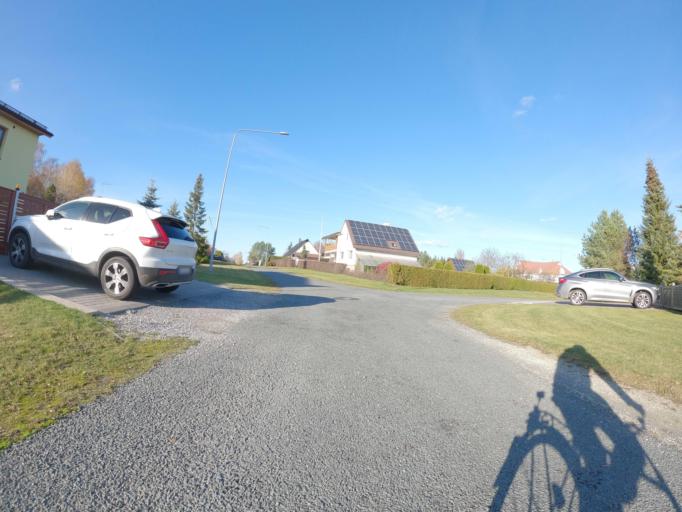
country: EE
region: Raplamaa
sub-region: Rapla vald
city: Rapla
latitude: 59.0102
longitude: 24.8095
